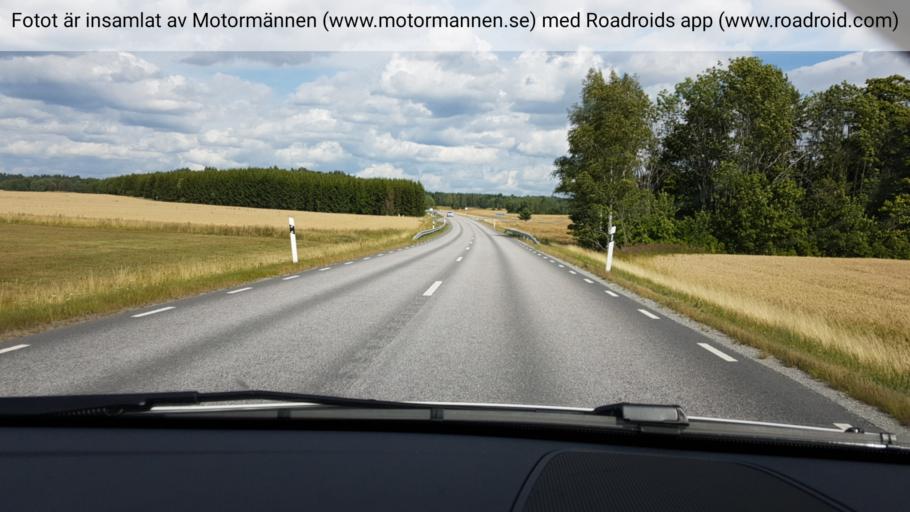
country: SE
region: Stockholm
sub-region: Vallentuna Kommun
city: Vallentuna
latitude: 59.6915
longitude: 18.0446
